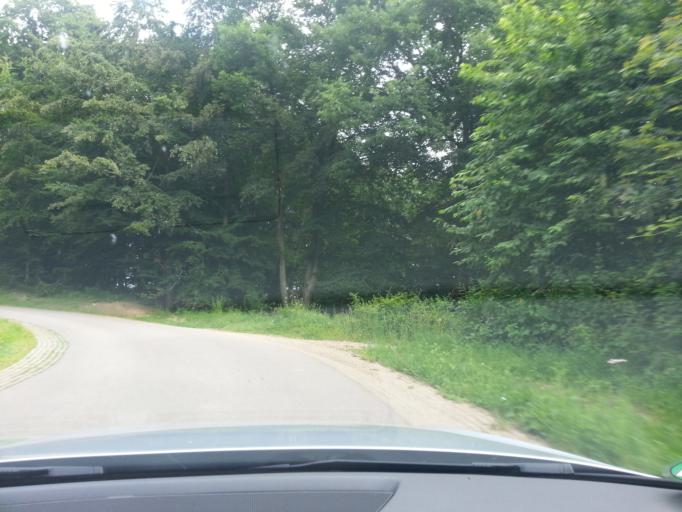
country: DE
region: Saarland
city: Tholey
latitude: 49.4910
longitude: 7.0502
